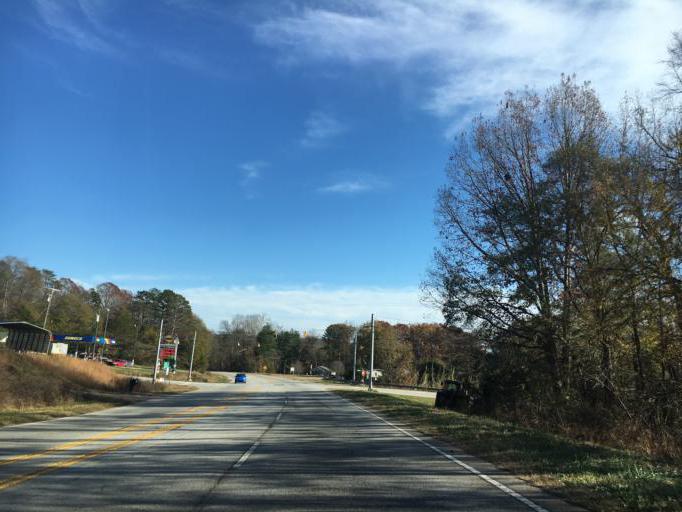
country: US
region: South Carolina
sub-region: Spartanburg County
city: Wellford
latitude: 34.9604
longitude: -82.0805
